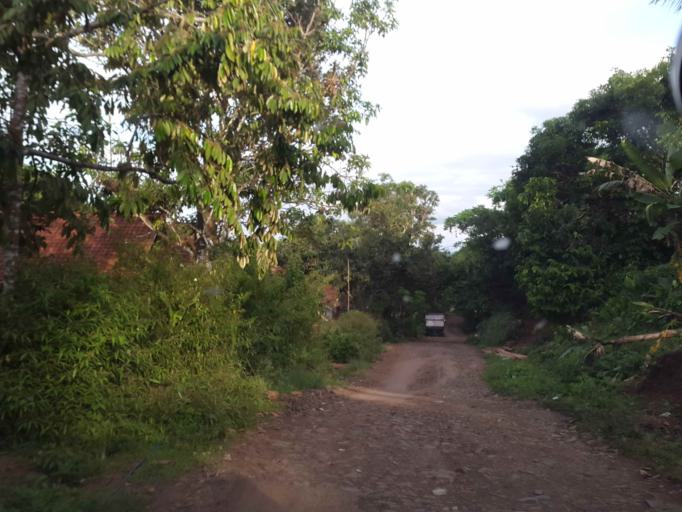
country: ID
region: Banten
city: Marapat
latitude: -6.6017
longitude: 105.7007
